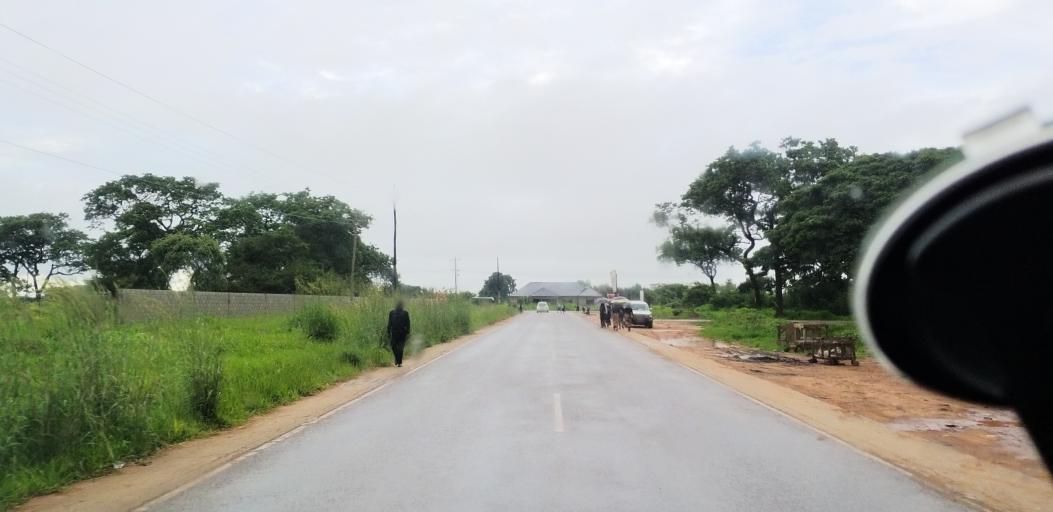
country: ZM
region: Lusaka
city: Lusaka
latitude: -15.5137
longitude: 28.3100
